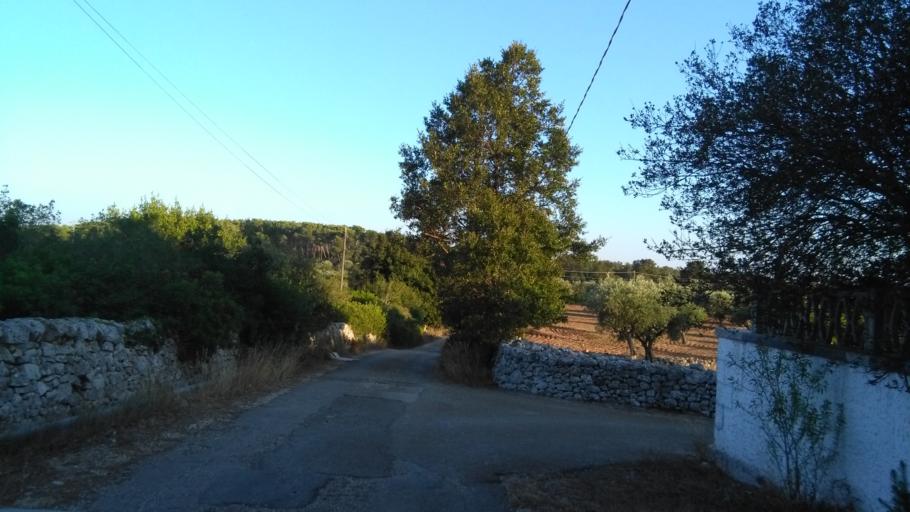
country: IT
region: Apulia
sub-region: Provincia di Bari
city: Putignano
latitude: 40.8278
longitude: 17.0772
